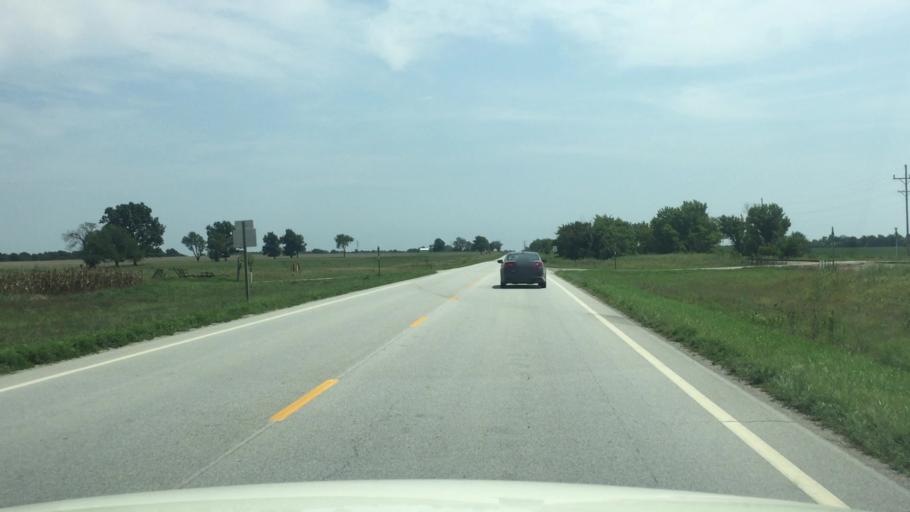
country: US
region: Kansas
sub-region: Cherokee County
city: Columbus
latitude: 37.1792
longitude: -94.9234
